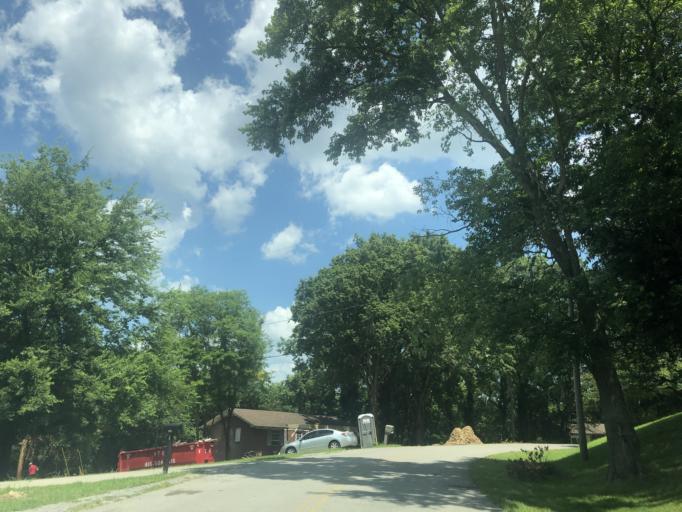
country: US
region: Tennessee
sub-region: Davidson County
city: Nashville
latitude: 36.1767
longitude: -86.6965
